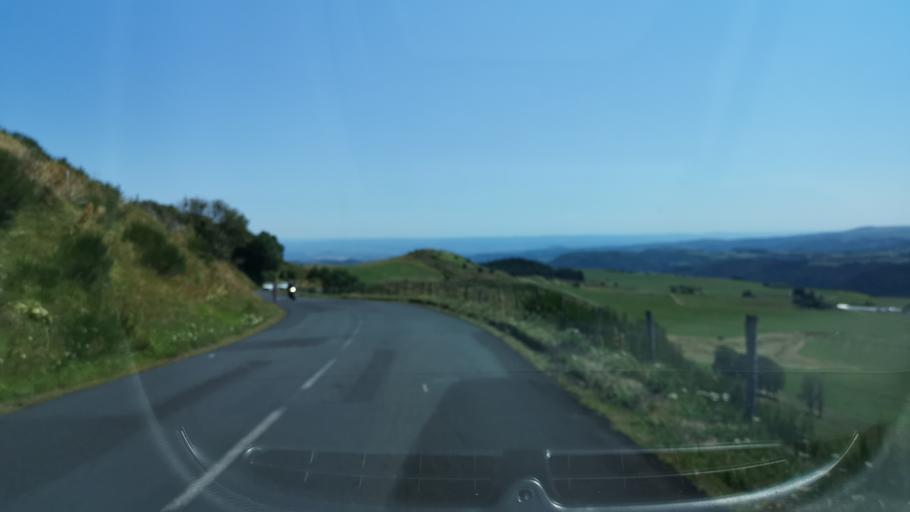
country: FR
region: Auvergne
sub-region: Departement du Puy-de-Dome
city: Mont-Dore
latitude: 45.5898
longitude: 2.8688
